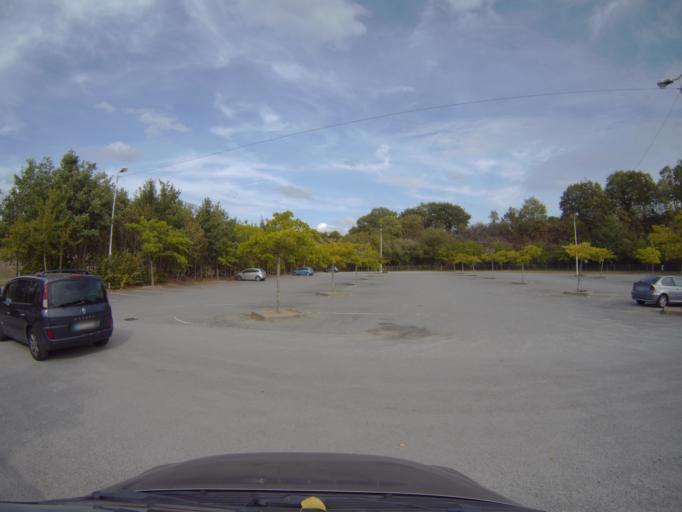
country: FR
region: Pays de la Loire
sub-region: Departement de la Loire-Atlantique
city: Saint-Herblain
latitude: 47.2104
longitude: -1.6348
